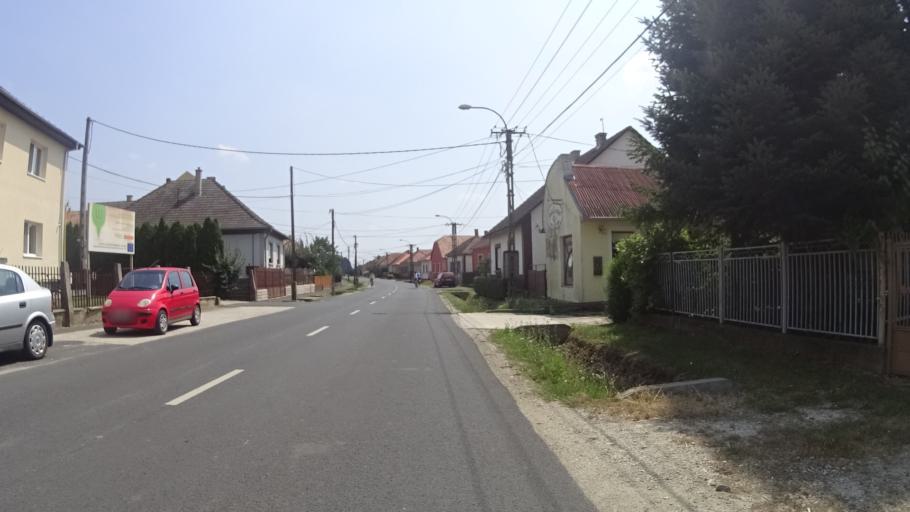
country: HU
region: Zala
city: Letenye
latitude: 46.4254
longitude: 16.7278
